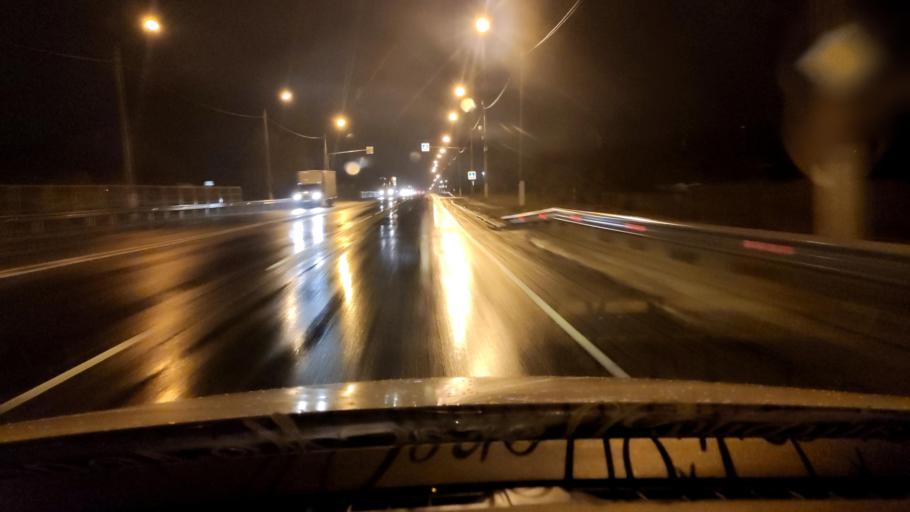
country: RU
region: Voronezj
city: Devitsa
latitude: 51.6359
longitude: 38.9351
